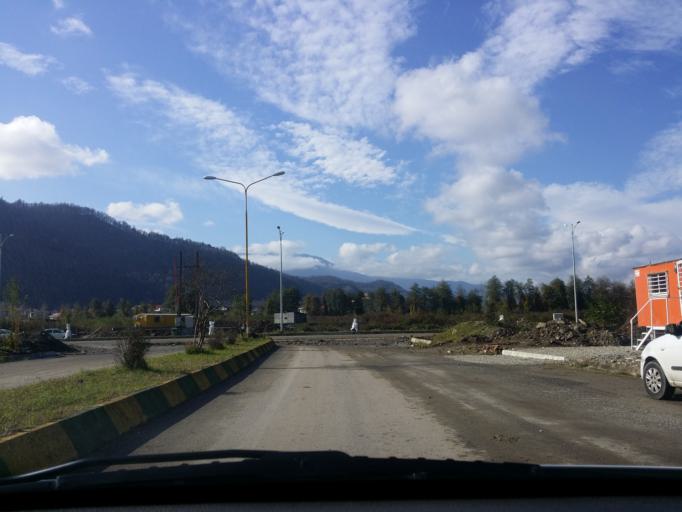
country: IR
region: Mazandaran
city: Chalus
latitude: 36.6756
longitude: 51.3003
